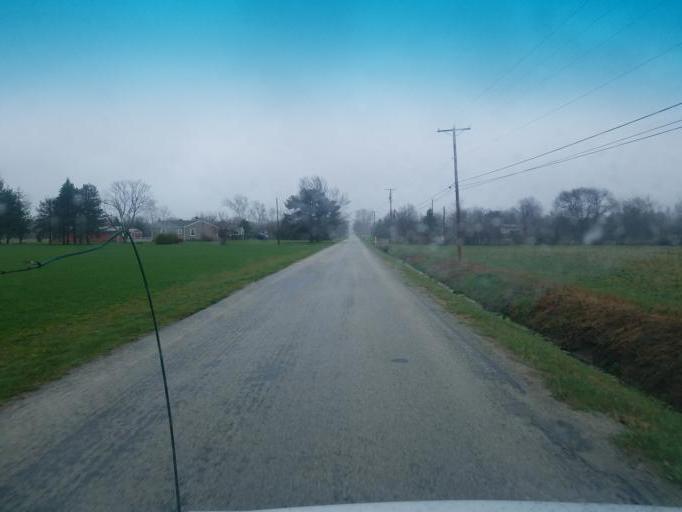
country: US
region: Ohio
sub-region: Wood County
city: North Baltimore
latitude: 41.2482
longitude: -83.6308
